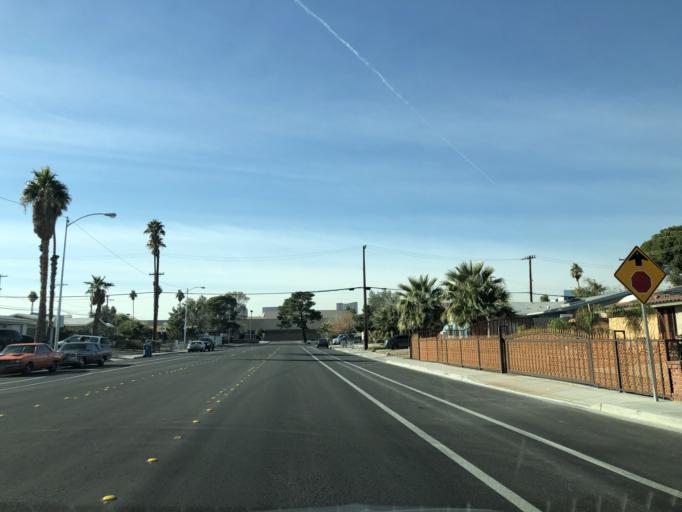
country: US
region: Nevada
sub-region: Clark County
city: Winchester
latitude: 36.1271
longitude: -115.1329
